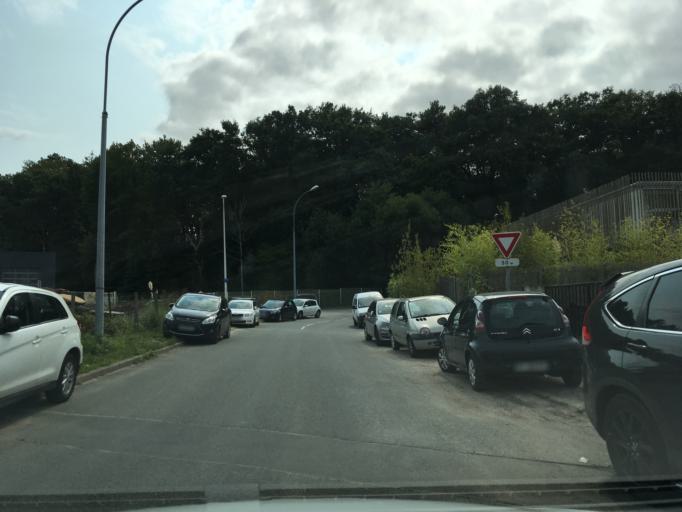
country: FR
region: Aquitaine
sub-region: Departement des Pyrenees-Atlantiques
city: Biarritz
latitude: 43.4635
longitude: -1.5418
